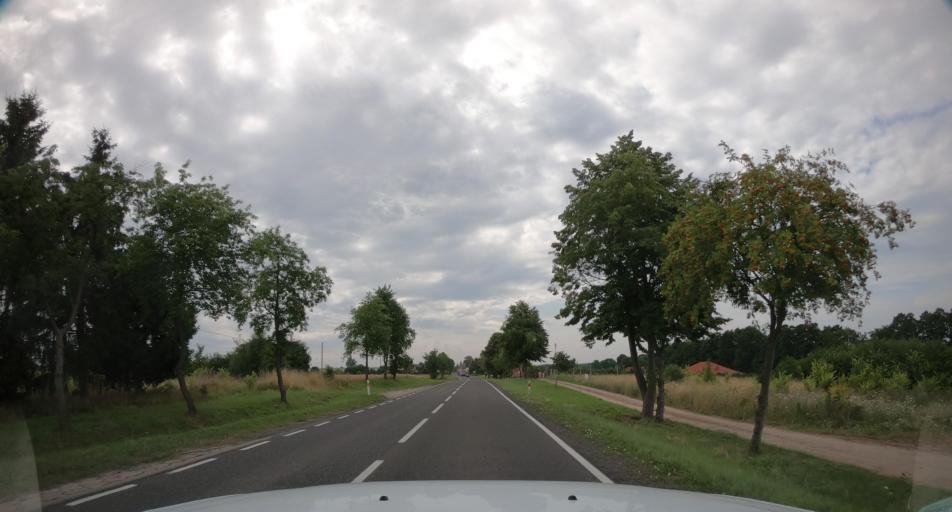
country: PL
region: West Pomeranian Voivodeship
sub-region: Powiat walecki
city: Walcz
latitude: 53.2461
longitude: 16.3949
